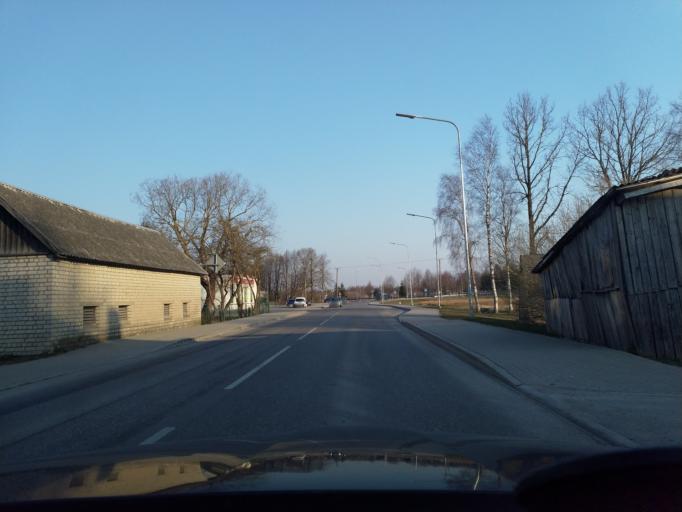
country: LV
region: Grobina
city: Grobina
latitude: 56.5351
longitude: 21.1890
